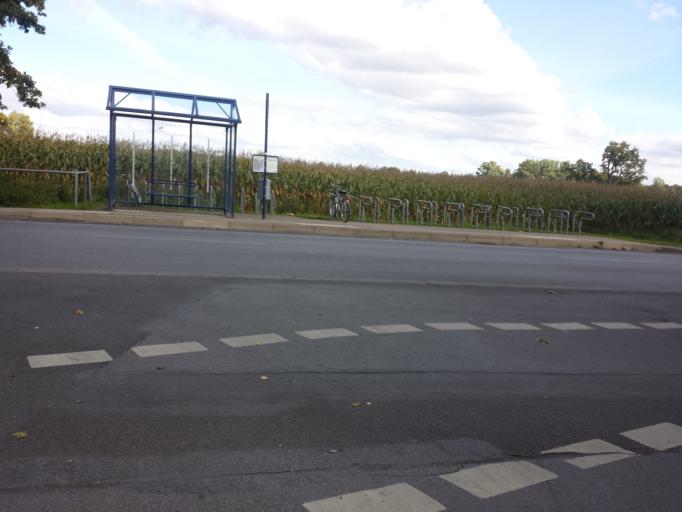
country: DE
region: North Rhine-Westphalia
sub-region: Regierungsbezirk Detmold
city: Langenberg
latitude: 51.7634
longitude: 8.3208
